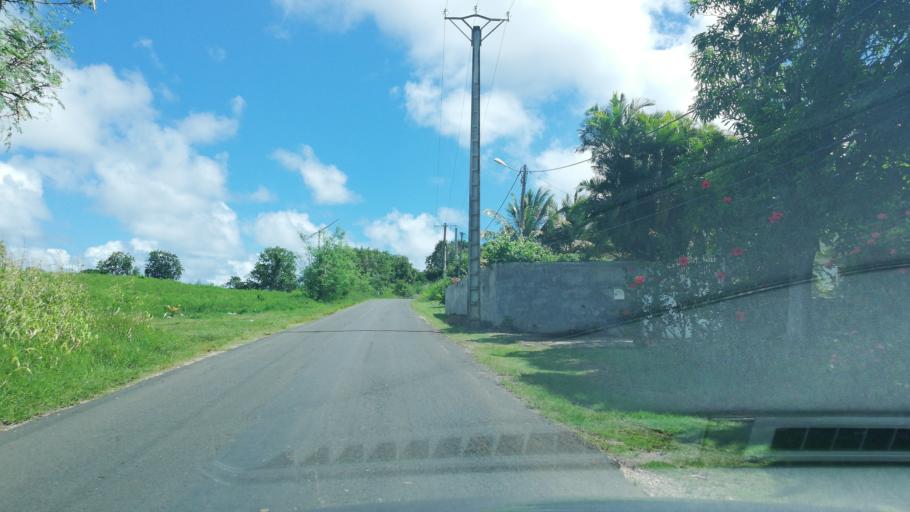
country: GP
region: Guadeloupe
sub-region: Guadeloupe
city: Petit-Canal
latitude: 16.3807
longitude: -61.4326
